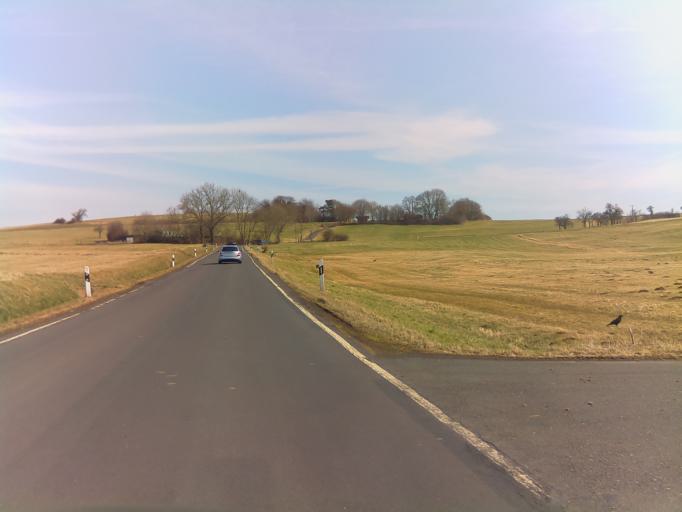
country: DE
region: Hesse
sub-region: Regierungsbezirk Giessen
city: Schwalmtal
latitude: 50.6518
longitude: 9.1925
